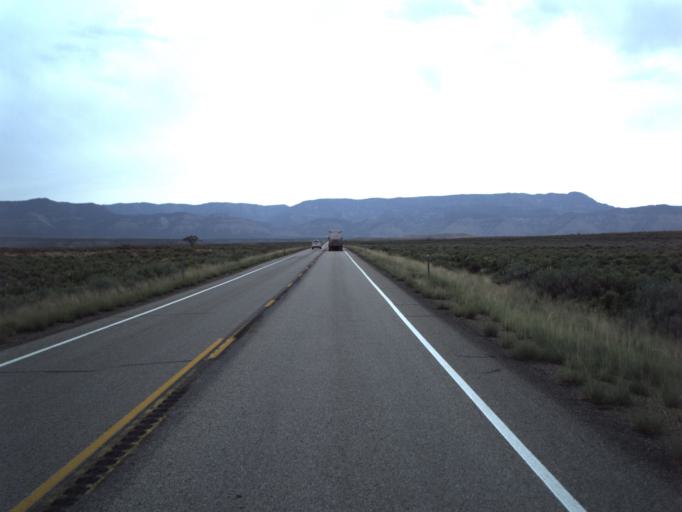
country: US
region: Utah
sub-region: Carbon County
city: East Carbon City
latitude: 39.5303
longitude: -110.5628
